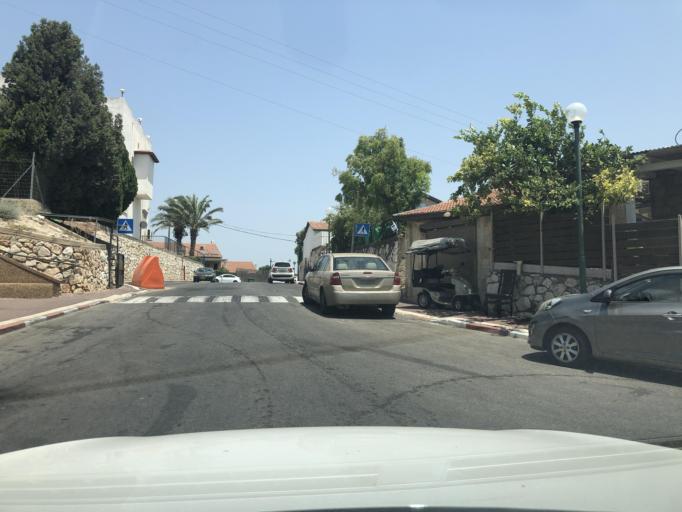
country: IL
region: Haifa
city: Daliyat el Karmil
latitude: 32.6588
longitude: 35.1106
